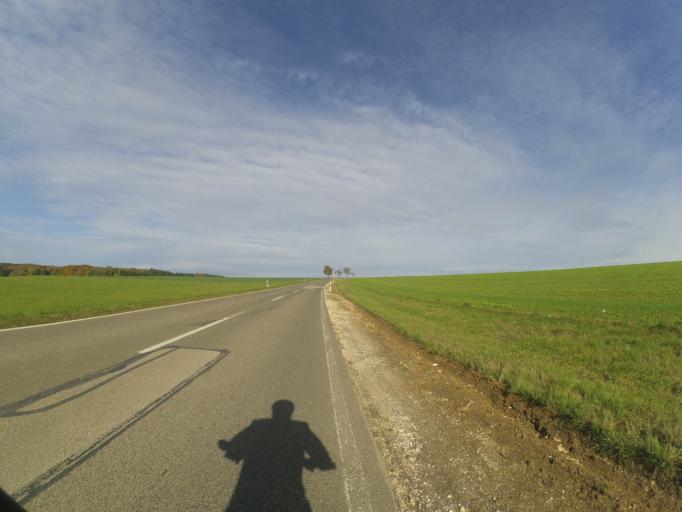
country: DE
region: Baden-Wuerttemberg
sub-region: Tuebingen Region
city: Lonsee
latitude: 48.5712
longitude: 9.9199
